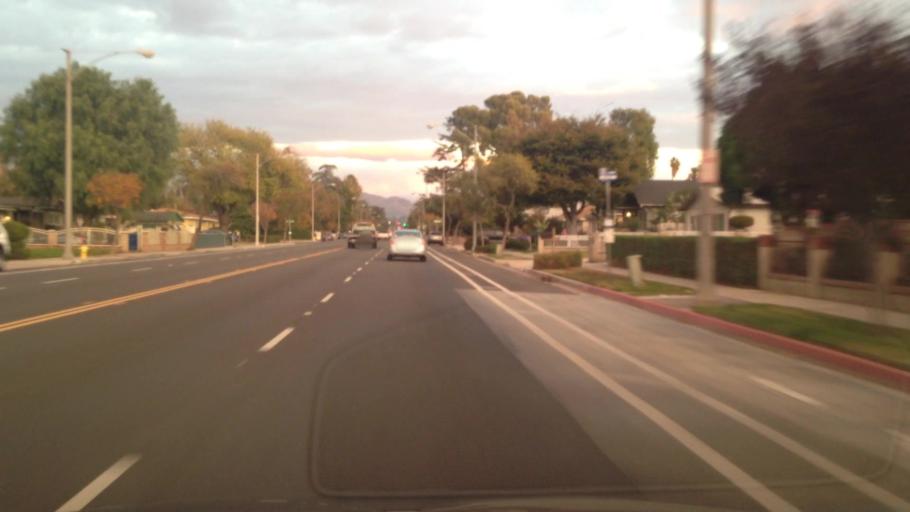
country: US
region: California
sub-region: Riverside County
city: Riverside
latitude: 33.9534
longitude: -117.4071
